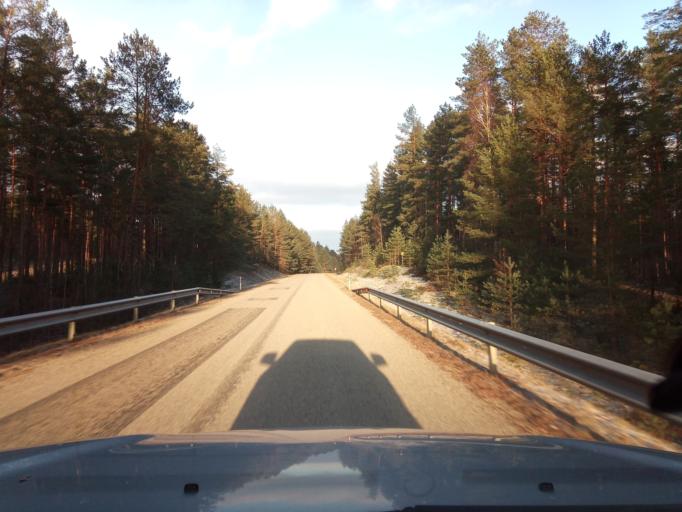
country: LT
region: Alytaus apskritis
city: Varena
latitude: 54.1232
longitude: 24.4529
